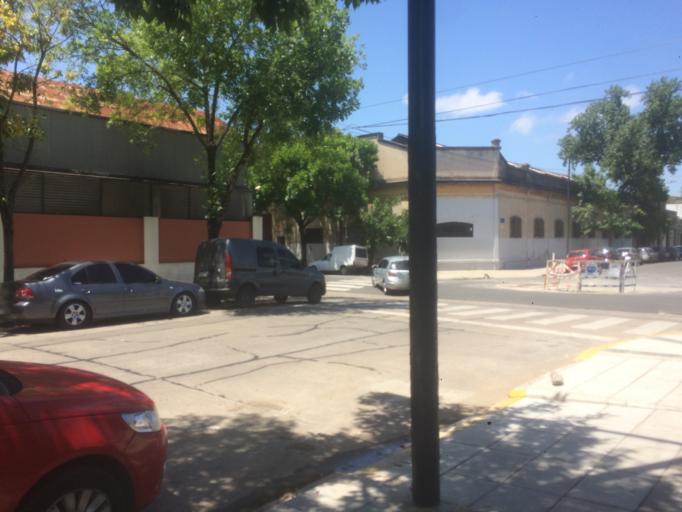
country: AR
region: Buenos Aires
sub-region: Partido de Avellaneda
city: Avellaneda
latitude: -34.6411
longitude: -58.3709
